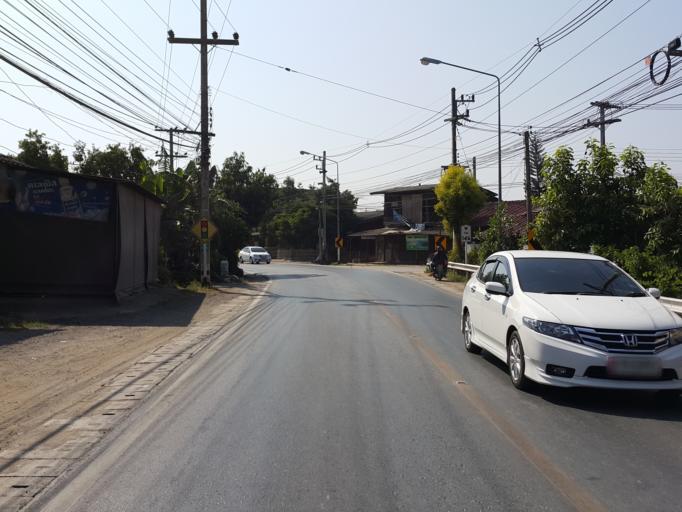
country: TH
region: Lamphun
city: Pa Sang
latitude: 18.5411
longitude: 98.9387
